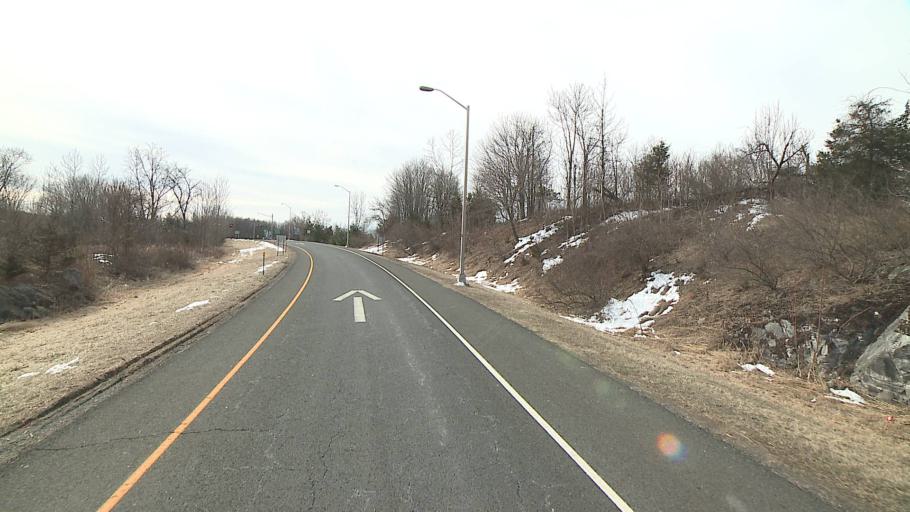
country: US
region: Connecticut
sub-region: Fairfield County
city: Danbury
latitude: 41.4727
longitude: -73.4099
